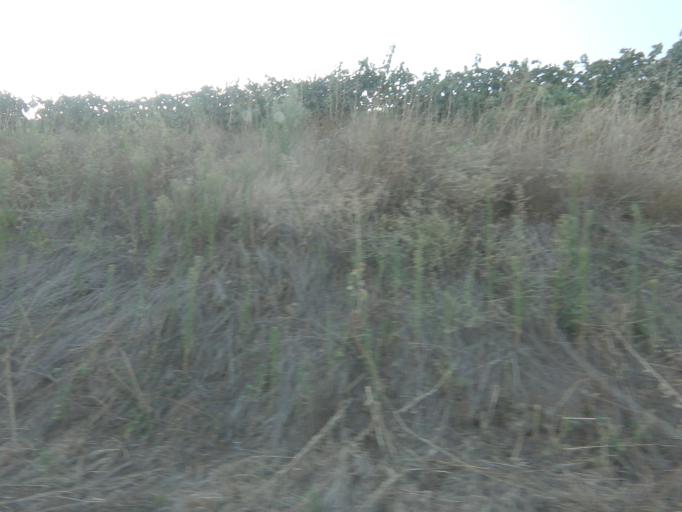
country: PT
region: Vila Real
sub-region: Sabrosa
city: Sabrosa
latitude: 41.2674
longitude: -7.5444
